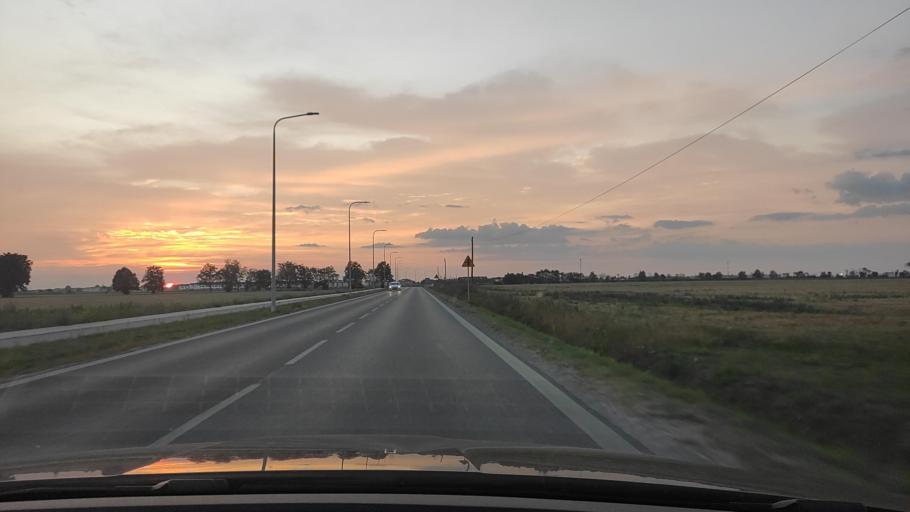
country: PL
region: Greater Poland Voivodeship
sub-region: Powiat poznanski
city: Swarzedz
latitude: 52.3773
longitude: 17.1070
